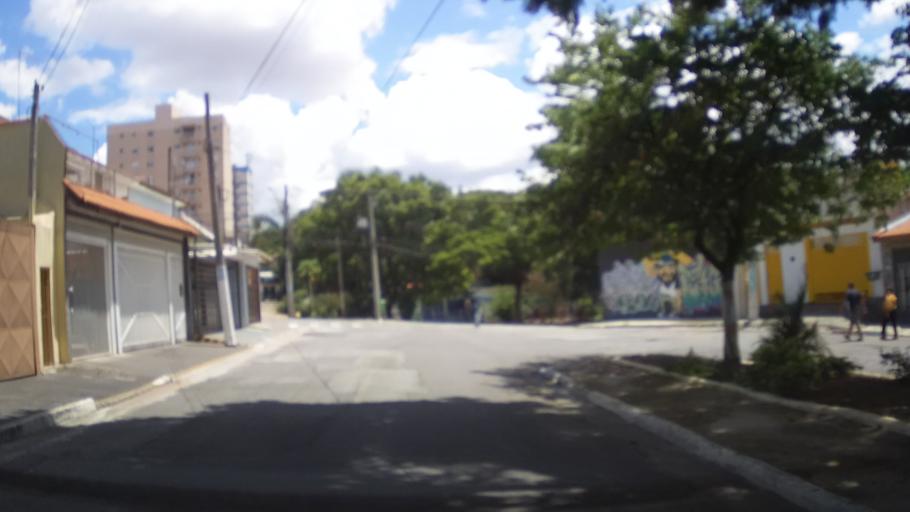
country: BR
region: Sao Paulo
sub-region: Guarulhos
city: Guarulhos
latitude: -23.4470
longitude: -46.5394
